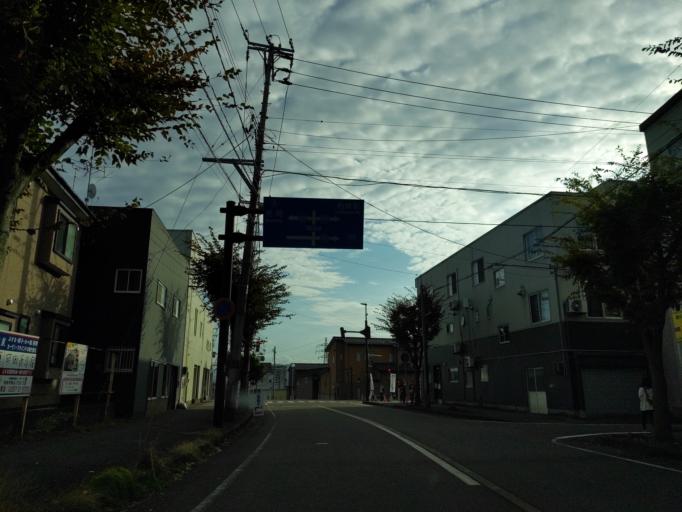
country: JP
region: Niigata
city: Kashiwazaki
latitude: 37.3706
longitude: 138.5604
